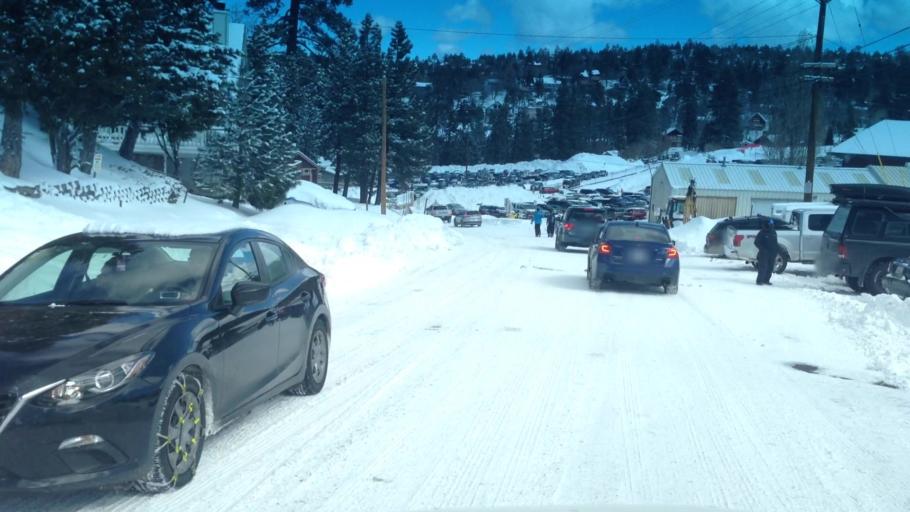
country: US
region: California
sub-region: San Bernardino County
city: Big Bear City
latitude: 34.2275
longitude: -116.8627
